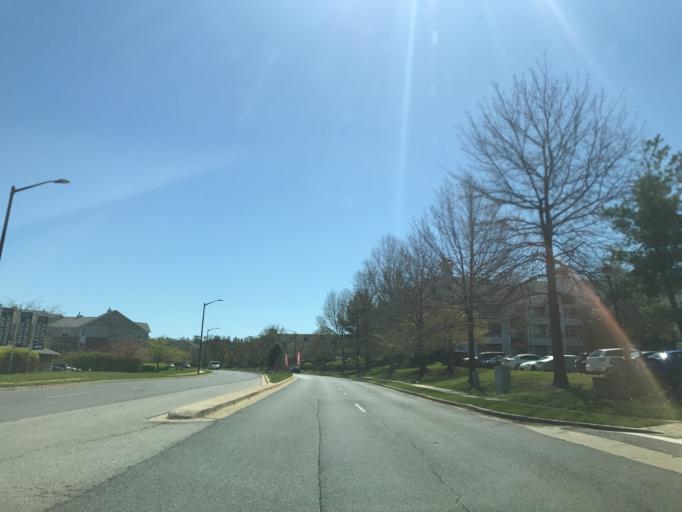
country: US
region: Maryland
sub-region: Anne Arundel County
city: Odenton
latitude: 39.0991
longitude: -76.7166
